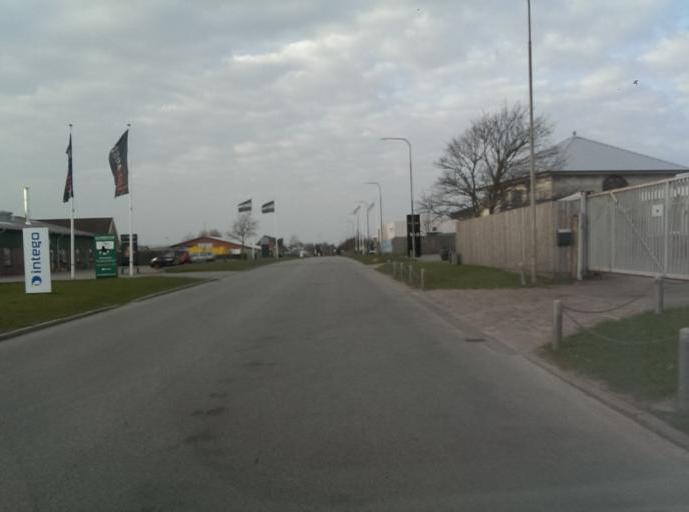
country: DK
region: South Denmark
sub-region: Esbjerg Kommune
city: Esbjerg
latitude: 55.5054
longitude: 8.4094
